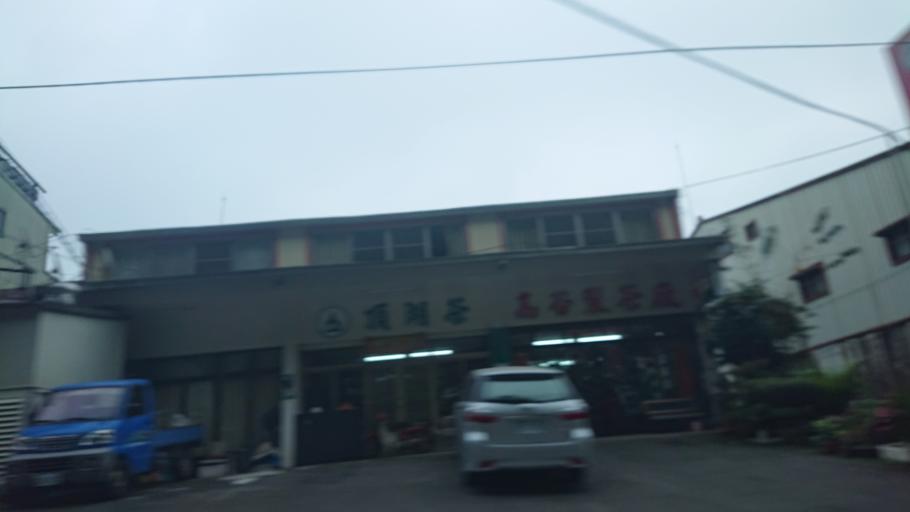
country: TW
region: Taiwan
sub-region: Chiayi
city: Jiayi Shi
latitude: 23.4712
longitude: 120.7071
